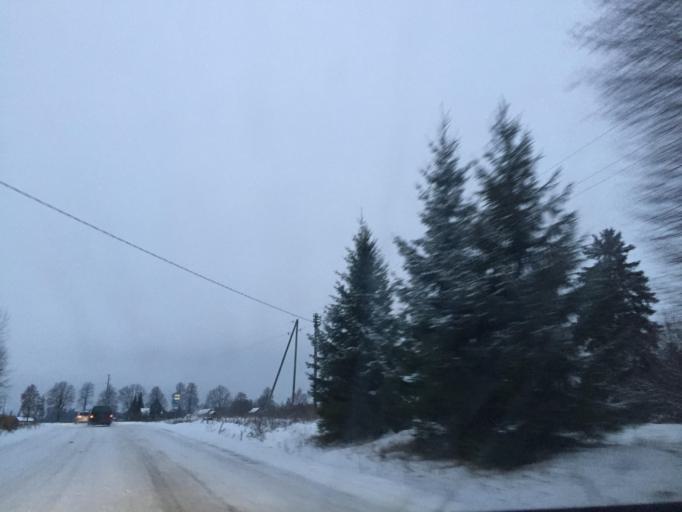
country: LV
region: Raunas
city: Rauna
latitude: 57.4317
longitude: 25.6216
